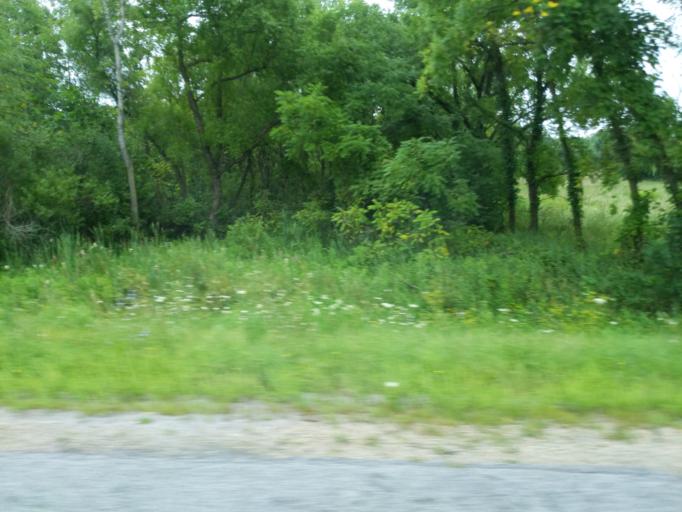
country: US
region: Wisconsin
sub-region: Sauk County
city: Sauk City
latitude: 43.2490
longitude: -89.7218
